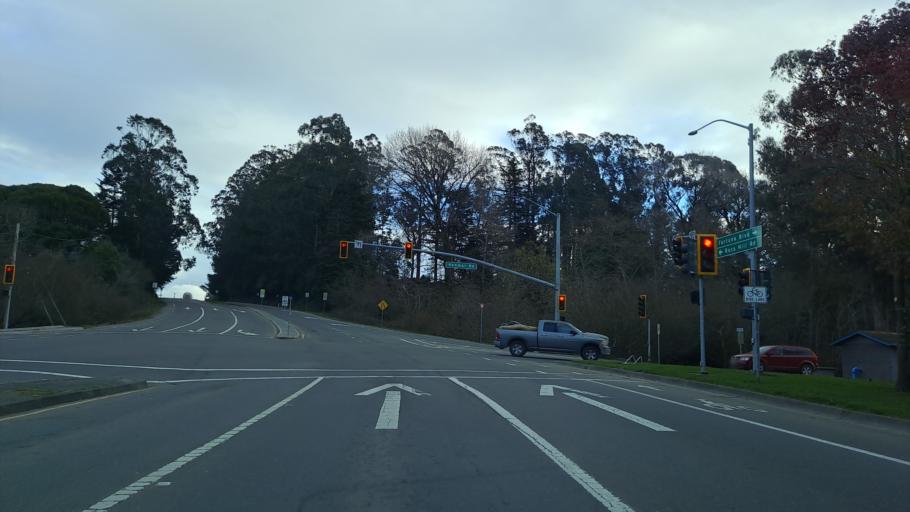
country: US
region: California
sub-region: Humboldt County
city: Fortuna
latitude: 40.5773
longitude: -124.1467
